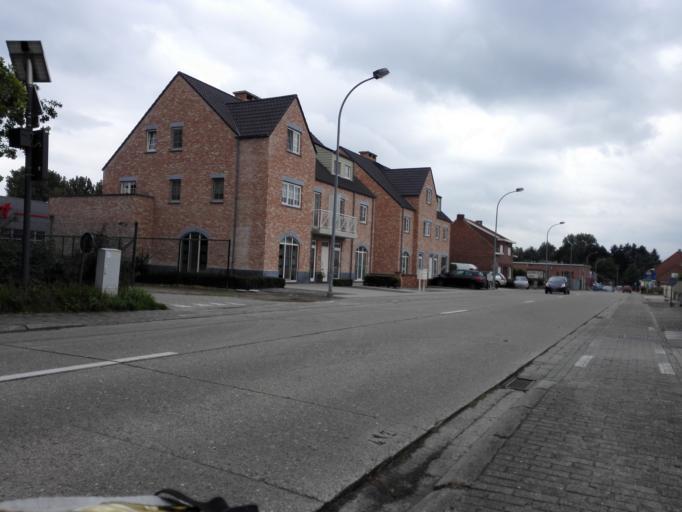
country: BE
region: Flanders
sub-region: Provincie Vlaams-Brabant
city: Tremelo
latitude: 50.9948
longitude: 4.7027
